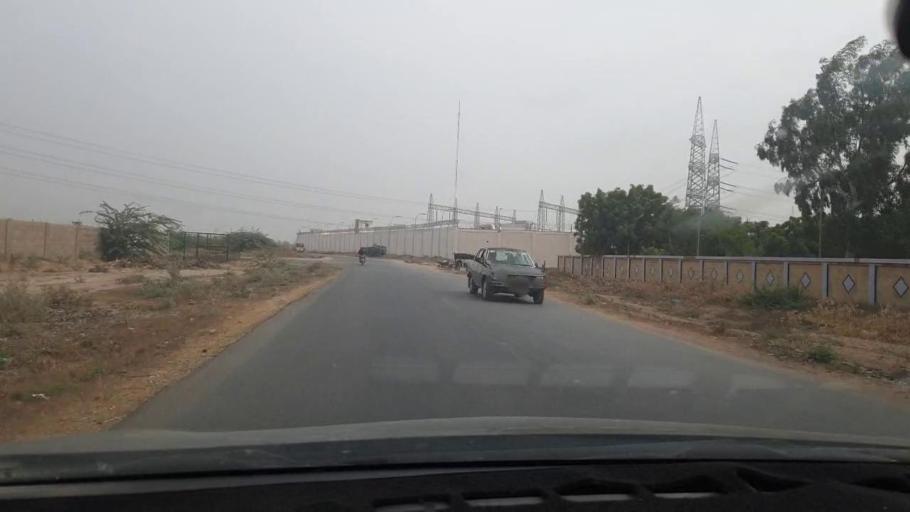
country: PK
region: Sindh
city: Malir Cantonment
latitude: 24.9118
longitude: 67.2808
